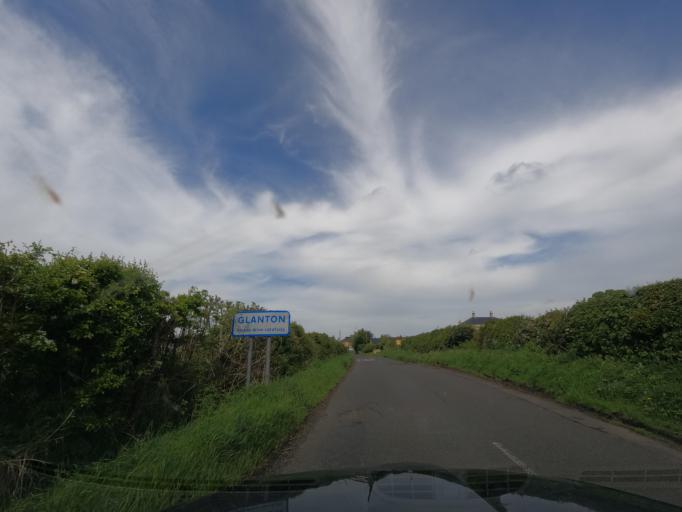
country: GB
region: England
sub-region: Northumberland
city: Whittingham
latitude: 55.4222
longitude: -1.8898
